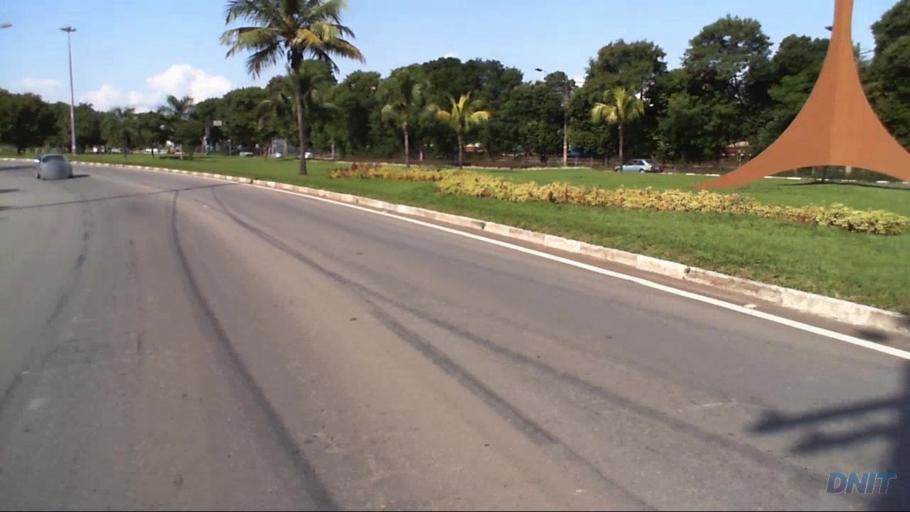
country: BR
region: Minas Gerais
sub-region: Ipatinga
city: Ipatinga
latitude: -19.4861
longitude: -42.5565
